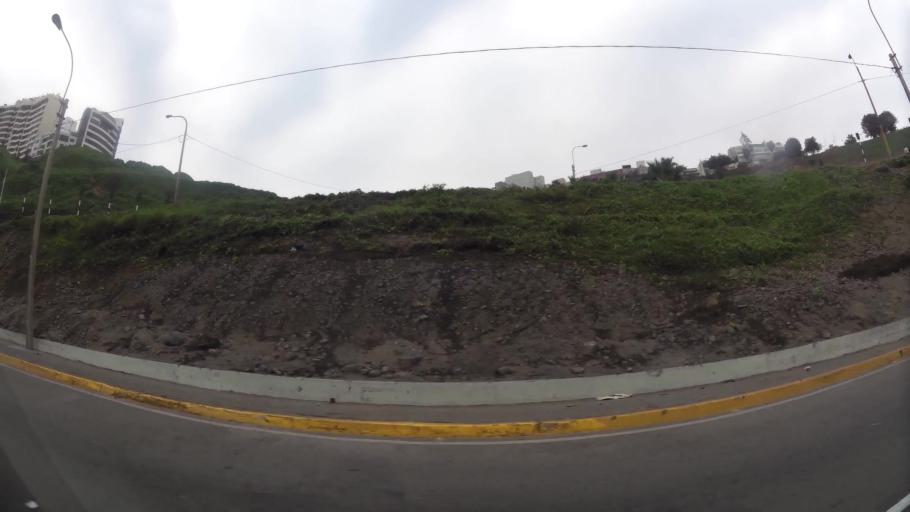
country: PE
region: Lima
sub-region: Lima
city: Surco
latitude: -12.1386
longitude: -77.0279
